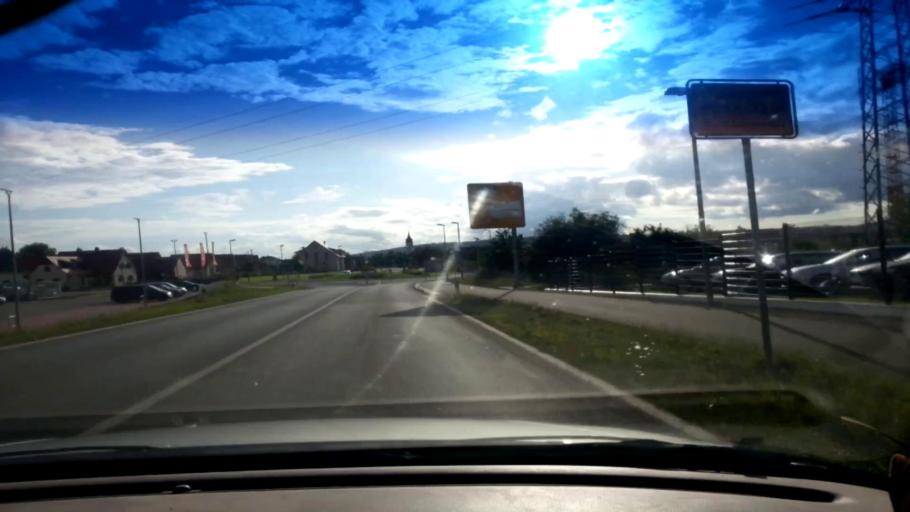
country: DE
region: Bavaria
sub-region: Upper Franconia
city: Ebensfeld
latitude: 50.0703
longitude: 10.9639
